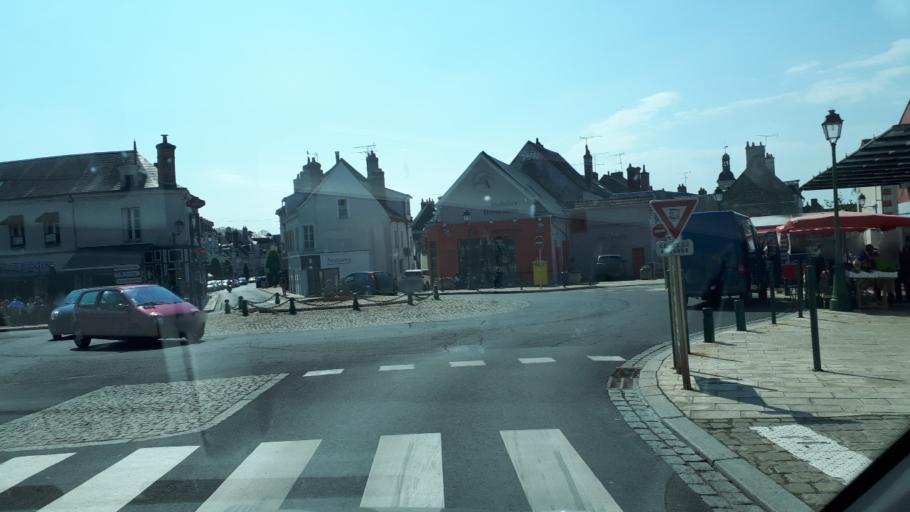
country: FR
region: Centre
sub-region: Departement du Loir-et-Cher
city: Romorantin-Lanthenay
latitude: 47.3613
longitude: 1.7426
